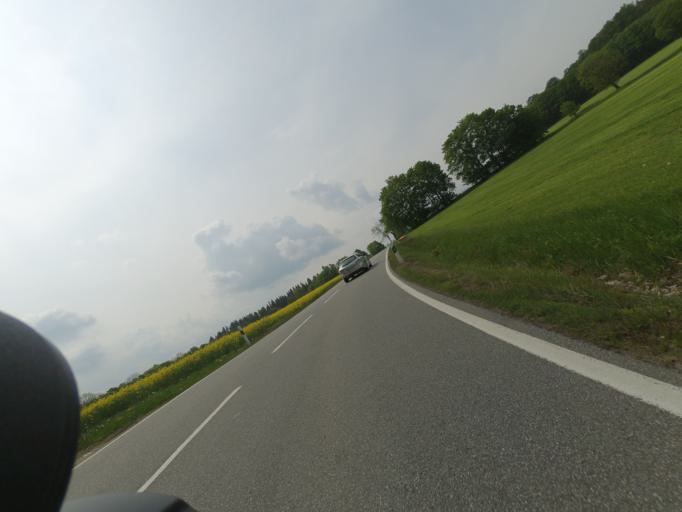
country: DE
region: Saxony
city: Olbernhau
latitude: 50.6520
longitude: 13.3061
